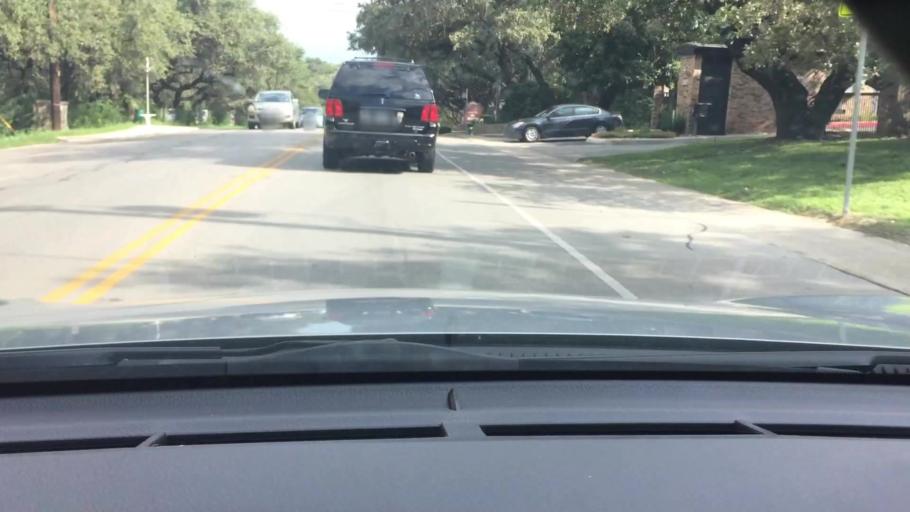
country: US
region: Texas
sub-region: Bexar County
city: Shavano Park
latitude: 29.5501
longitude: -98.5685
